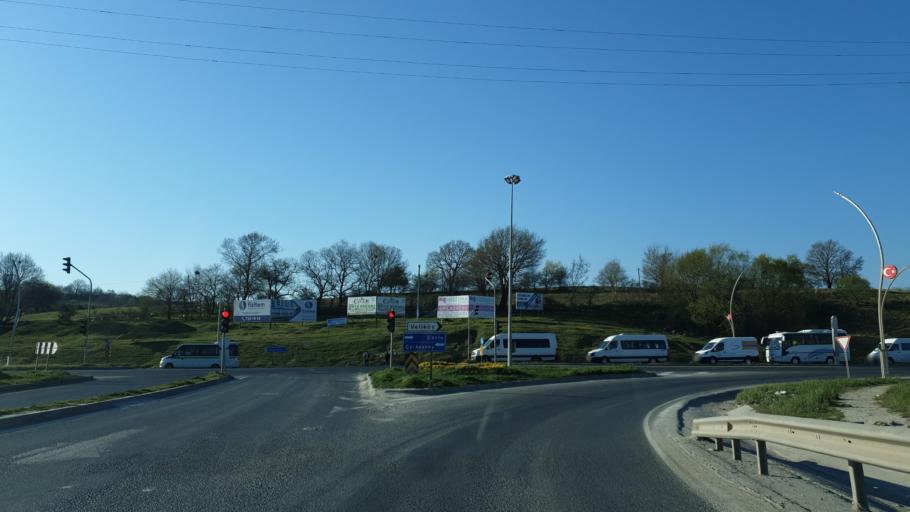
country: TR
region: Tekirdag
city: Cerkezkoey
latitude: 41.2759
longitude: 27.9865
